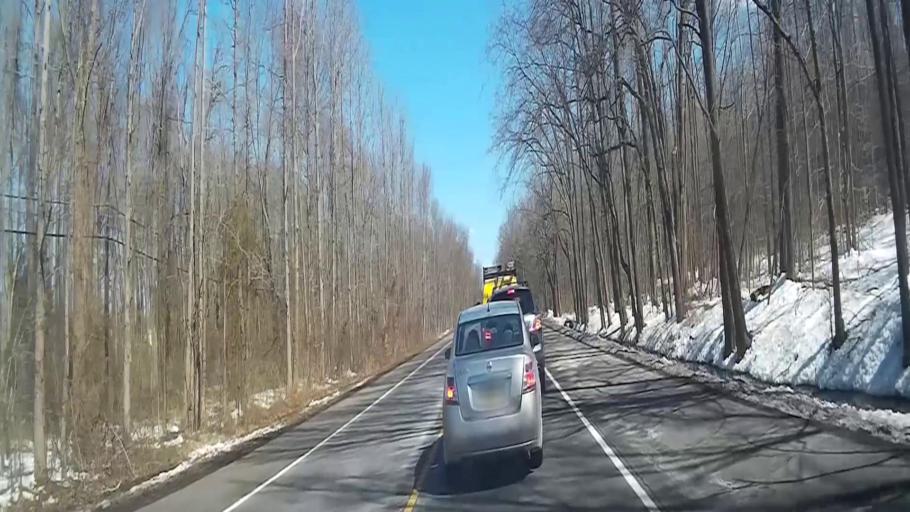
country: US
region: New Jersey
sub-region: Burlington County
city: Marlton
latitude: 39.8940
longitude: -74.8923
